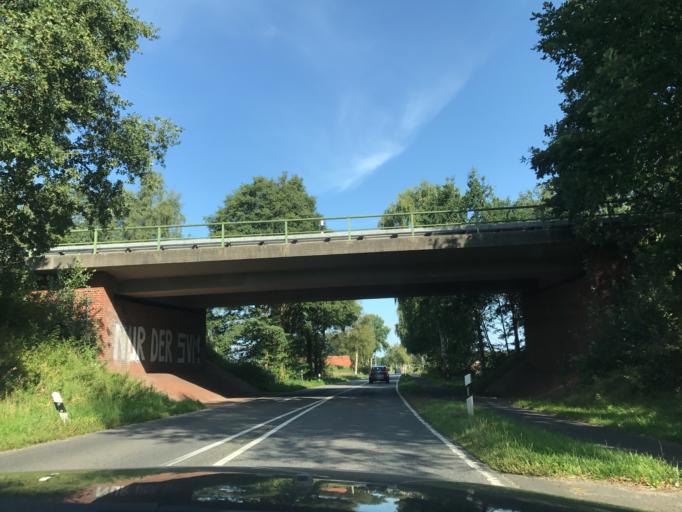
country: DE
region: Lower Saxony
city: Haselunne
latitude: 52.6878
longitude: 7.4722
